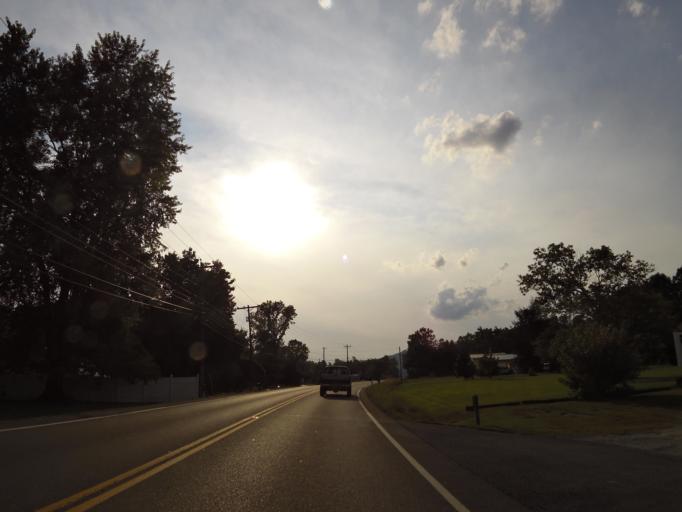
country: US
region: Tennessee
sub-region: Morgan County
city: Coalfield
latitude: 36.0336
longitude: -84.4170
